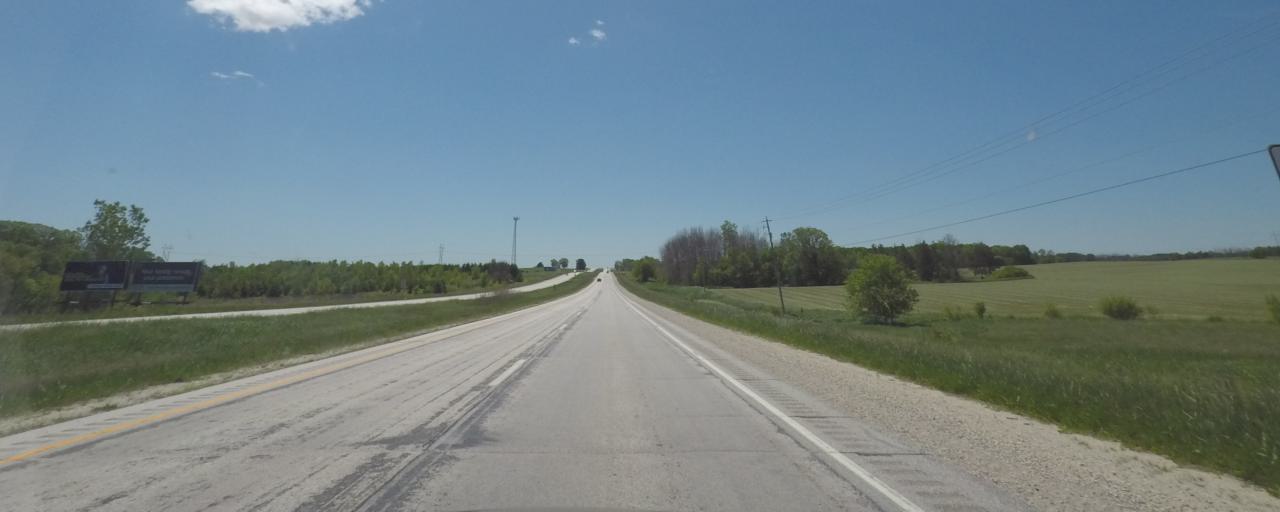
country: US
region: Wisconsin
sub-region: Sheboygan County
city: Plymouth
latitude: 43.7021
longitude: -87.9408
